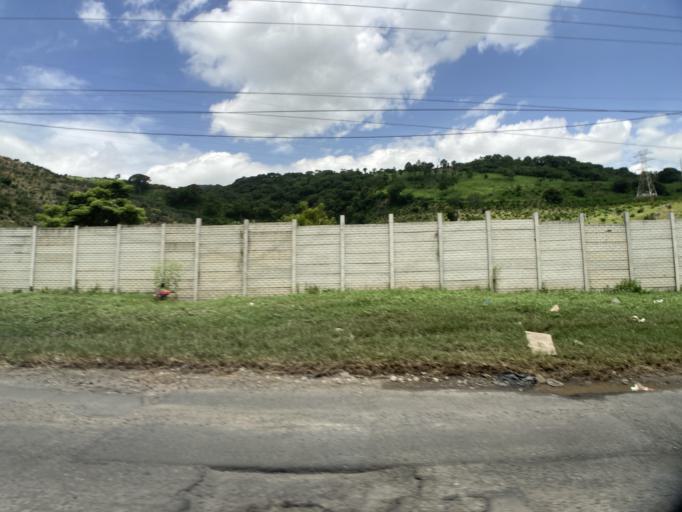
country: GT
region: Guatemala
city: Amatitlan
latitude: 14.4648
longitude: -90.5891
